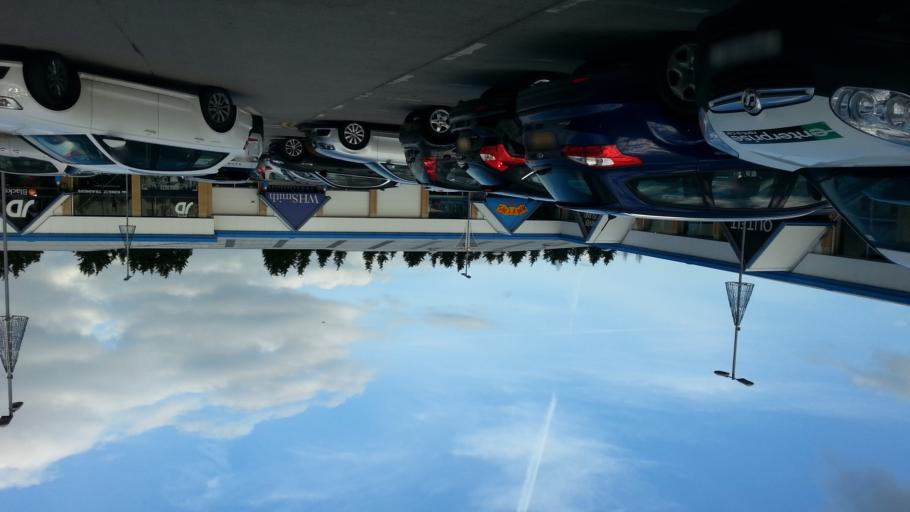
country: GB
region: England
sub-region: Staffordshire
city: Tamworth
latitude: 52.6267
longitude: -1.6998
